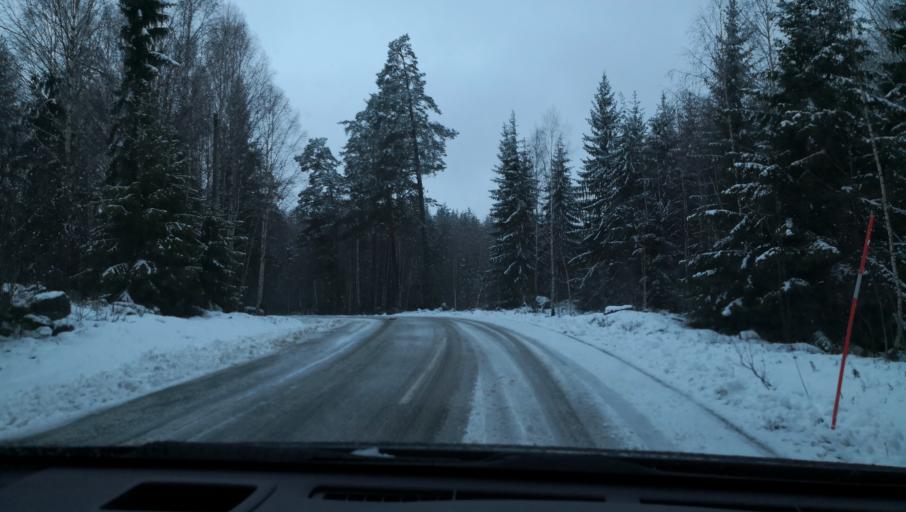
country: SE
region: Vaestmanland
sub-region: Kopings Kommun
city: Kolsva
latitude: 59.5685
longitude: 15.7877
